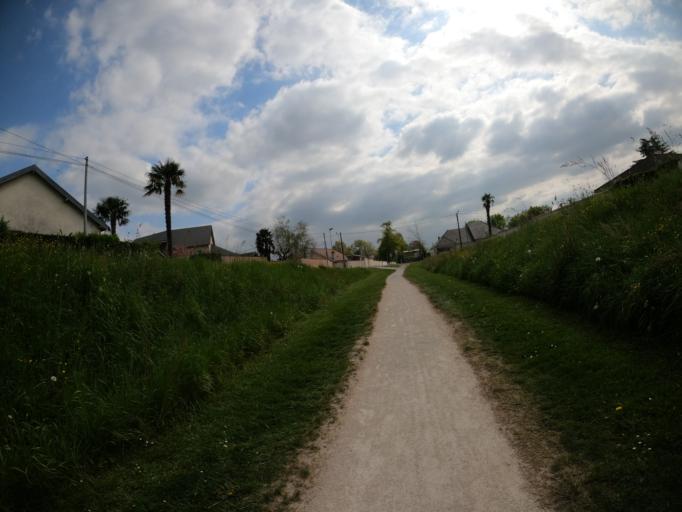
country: FR
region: Aquitaine
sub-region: Departement des Pyrenees-Atlantiques
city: Lons
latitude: 43.3258
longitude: -0.3837
